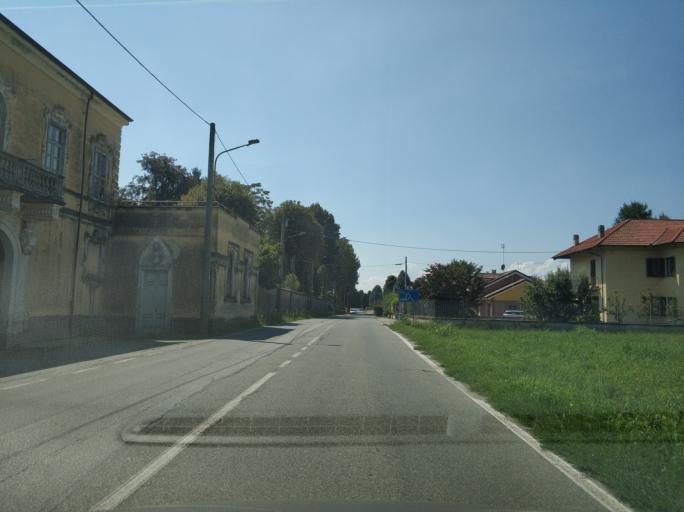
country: IT
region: Piedmont
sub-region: Provincia di Torino
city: San Maurizio
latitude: 45.2077
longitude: 7.6206
